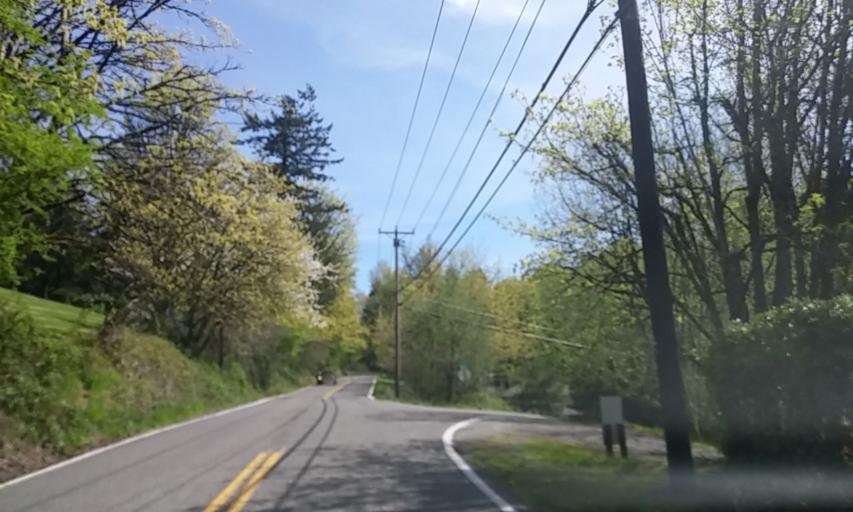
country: US
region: Oregon
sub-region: Washington County
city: West Haven-Sylvan
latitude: 45.5166
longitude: -122.7405
